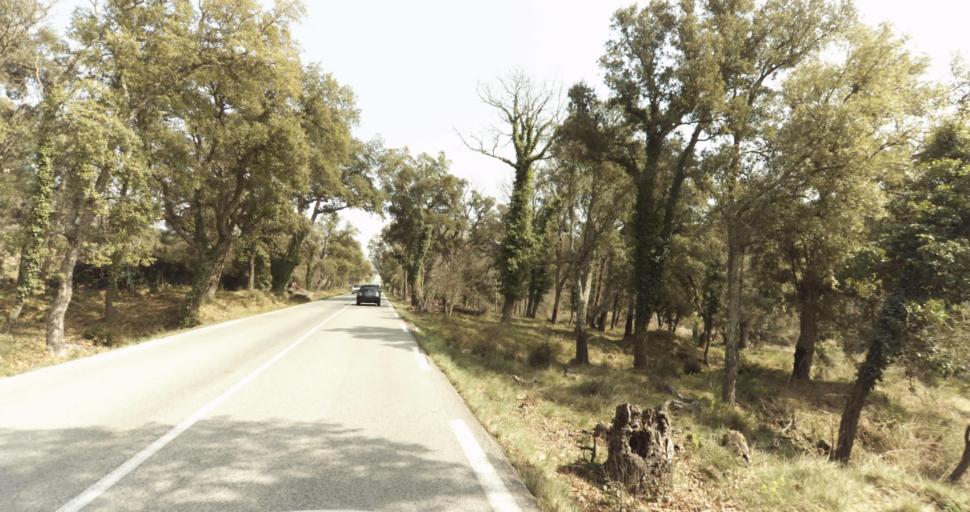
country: FR
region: Provence-Alpes-Cote d'Azur
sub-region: Departement du Var
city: Le Lavandou
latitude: 43.1993
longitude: 6.3950
